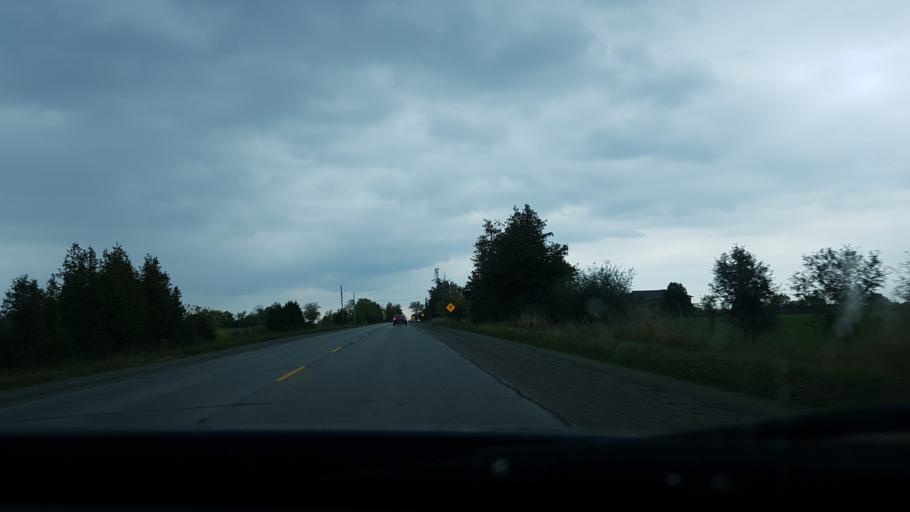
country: CA
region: Ontario
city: Omemee
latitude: 44.3753
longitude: -78.6494
